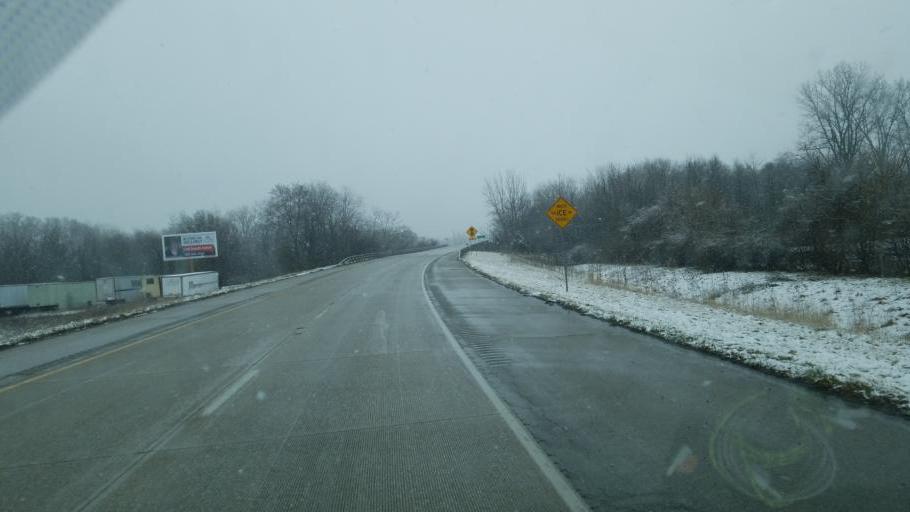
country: US
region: Indiana
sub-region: Grant County
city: Marion
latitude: 40.5575
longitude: -85.6490
